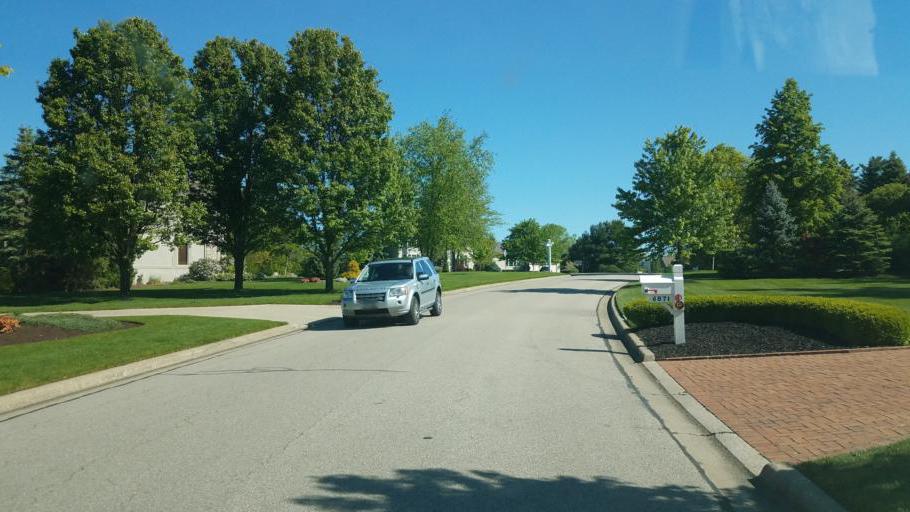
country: US
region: Ohio
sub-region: Franklin County
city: Westerville
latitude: 40.1654
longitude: -82.9489
